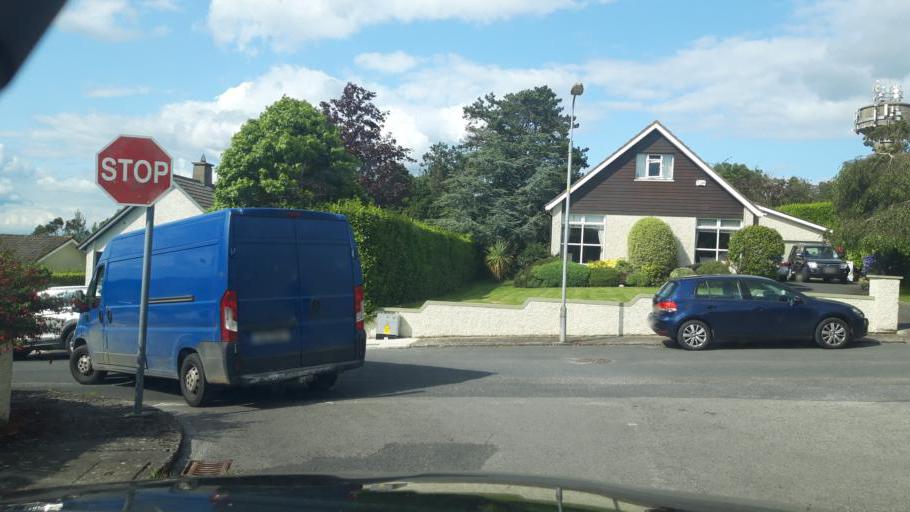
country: IE
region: Munster
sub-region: Waterford
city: Waterford
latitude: 52.2468
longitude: -7.0950
